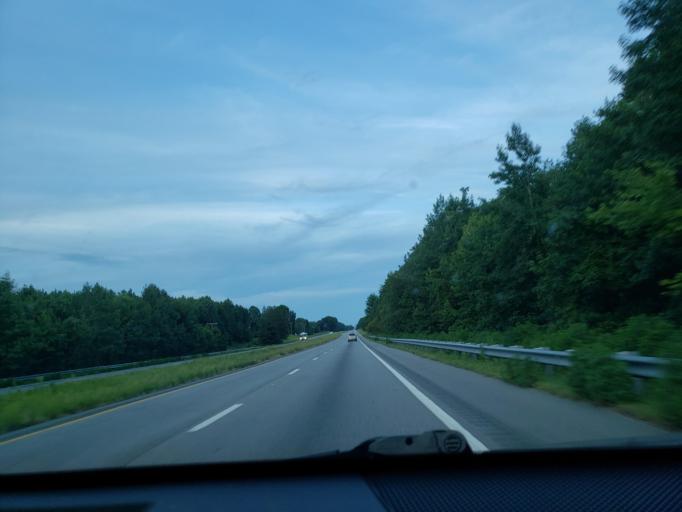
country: US
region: Virginia
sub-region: Southampton County
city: Courtland
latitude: 36.7037
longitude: -77.2223
